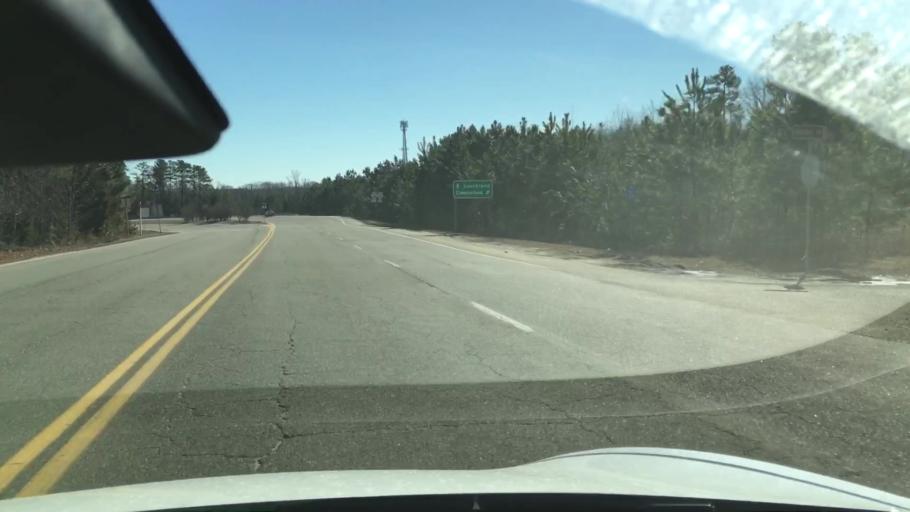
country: US
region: Virginia
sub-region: Henrico County
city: Short Pump
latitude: 37.5608
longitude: -77.6953
